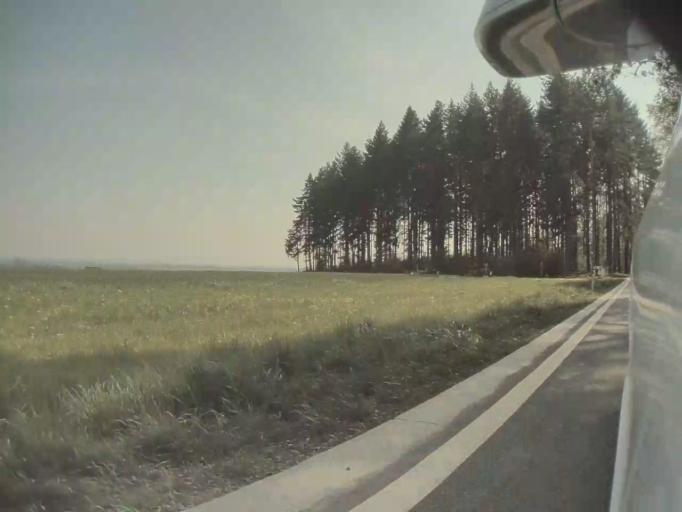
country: BE
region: Wallonia
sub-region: Province de Namur
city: Havelange
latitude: 50.3128
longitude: 5.2363
